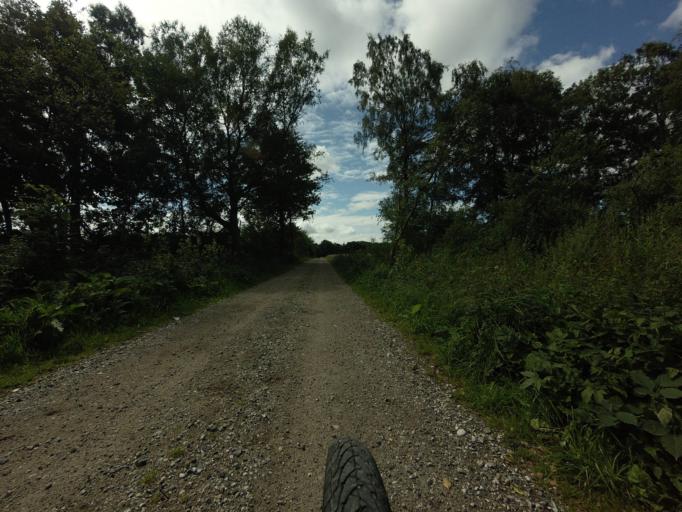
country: DK
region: Central Jutland
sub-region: Norddjurs Kommune
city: Auning
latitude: 56.4397
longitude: 10.3660
